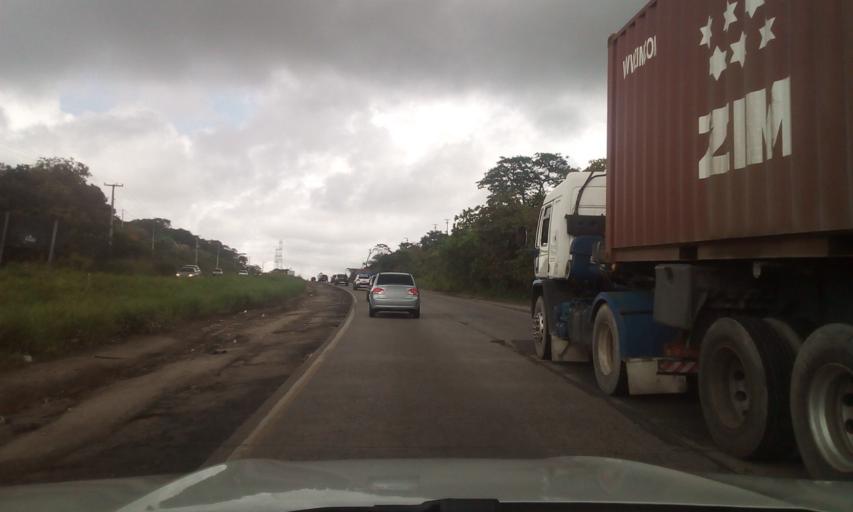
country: BR
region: Pernambuco
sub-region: Paulista
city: Paulista
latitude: -7.9489
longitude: -34.9074
